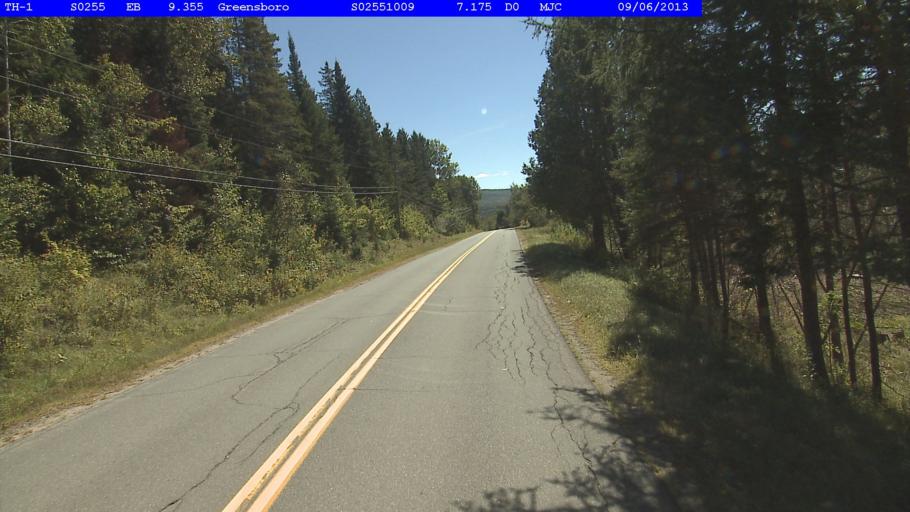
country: US
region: Vermont
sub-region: Caledonia County
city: Hardwick
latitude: 44.5523
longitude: -72.2718
